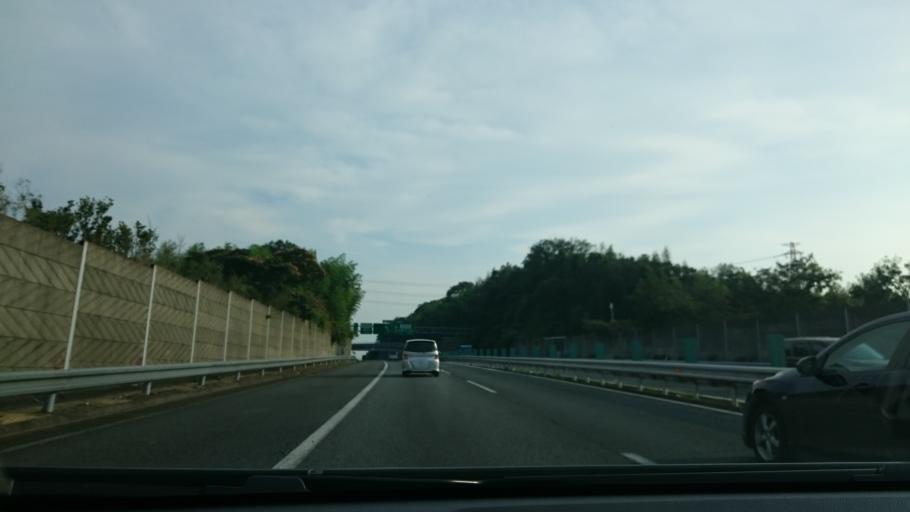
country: JP
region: Mie
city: Yokkaichi
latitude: 35.0479
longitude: 136.6341
